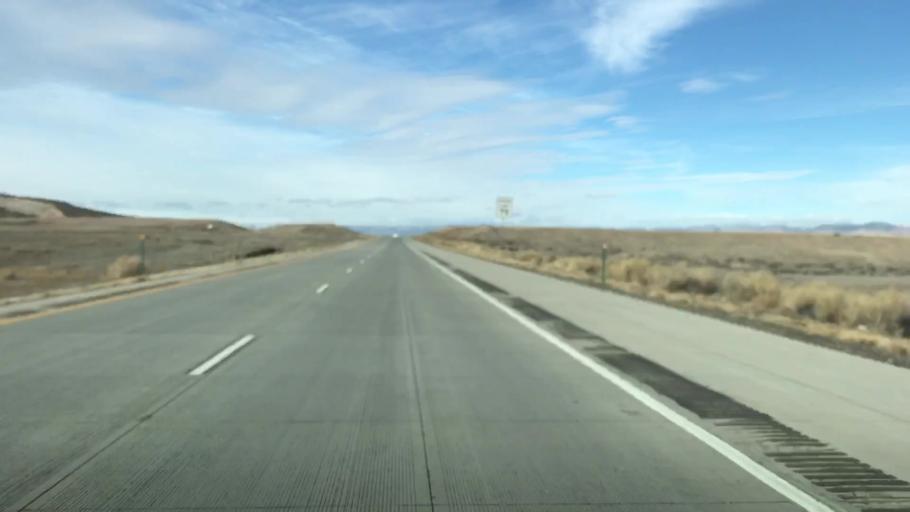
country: US
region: Colorado
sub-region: Mesa County
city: Loma
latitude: 39.1887
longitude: -108.8356
